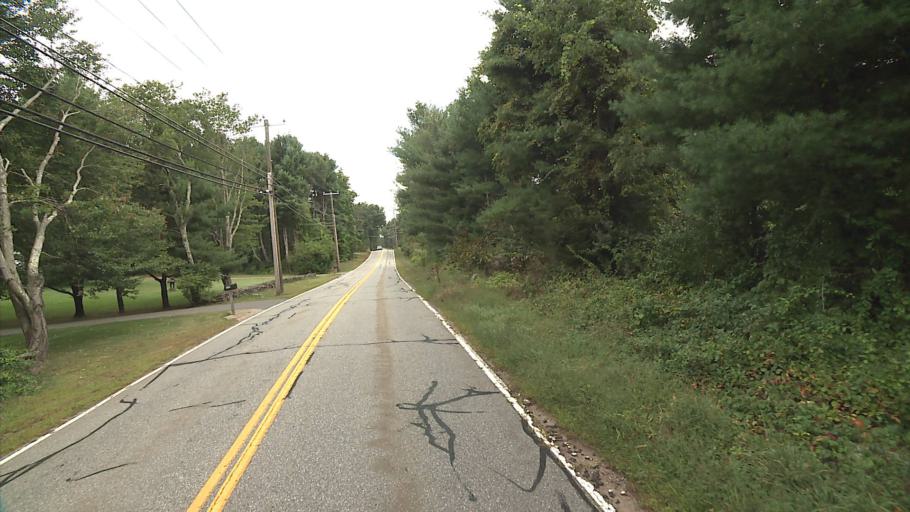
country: US
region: Connecticut
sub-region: Tolland County
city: Storrs
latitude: 41.8466
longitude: -72.2734
